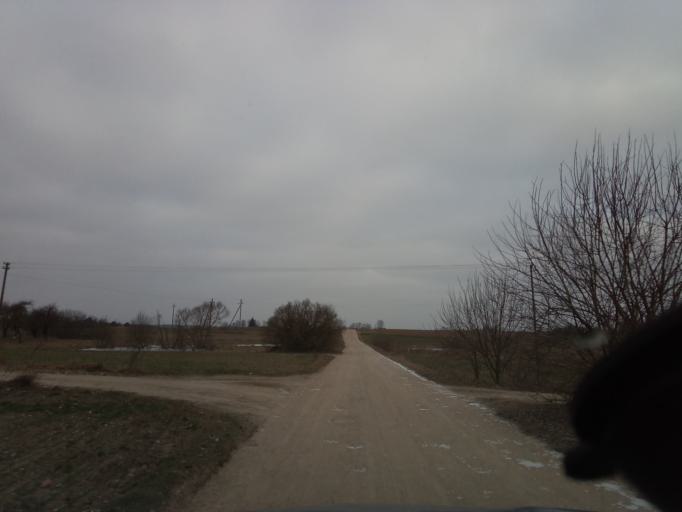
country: LT
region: Alytaus apskritis
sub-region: Alytaus rajonas
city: Daugai
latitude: 54.3754
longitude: 24.4417
